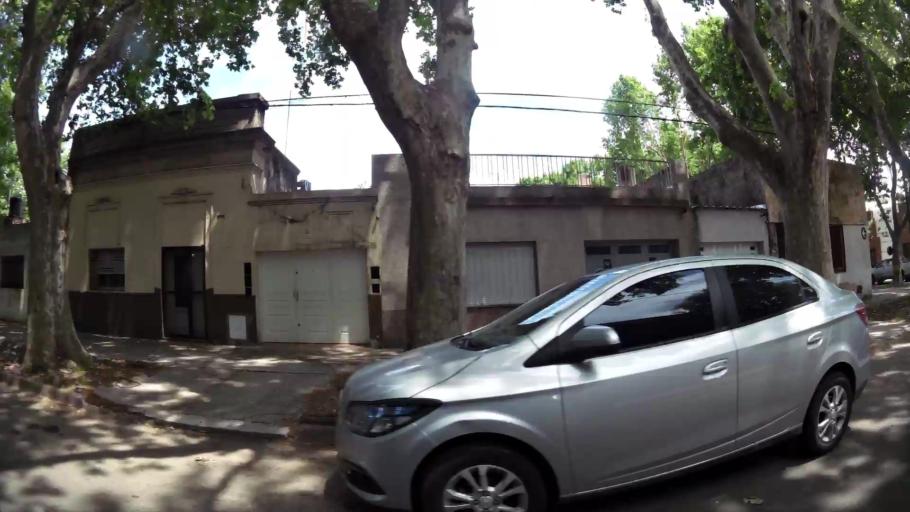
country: AR
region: Santa Fe
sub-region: Departamento de Rosario
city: Rosario
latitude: -32.9736
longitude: -60.6318
